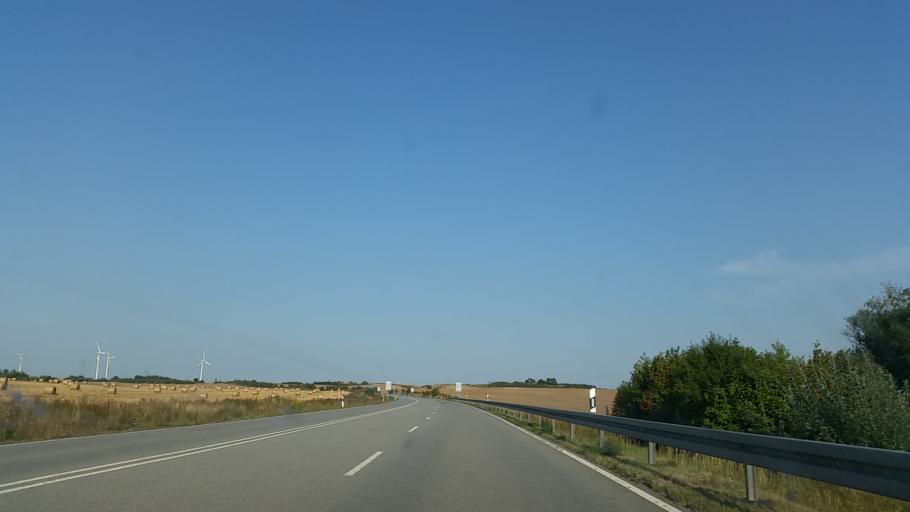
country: DE
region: Brandenburg
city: Schoneberg
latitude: 53.0742
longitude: 14.1549
